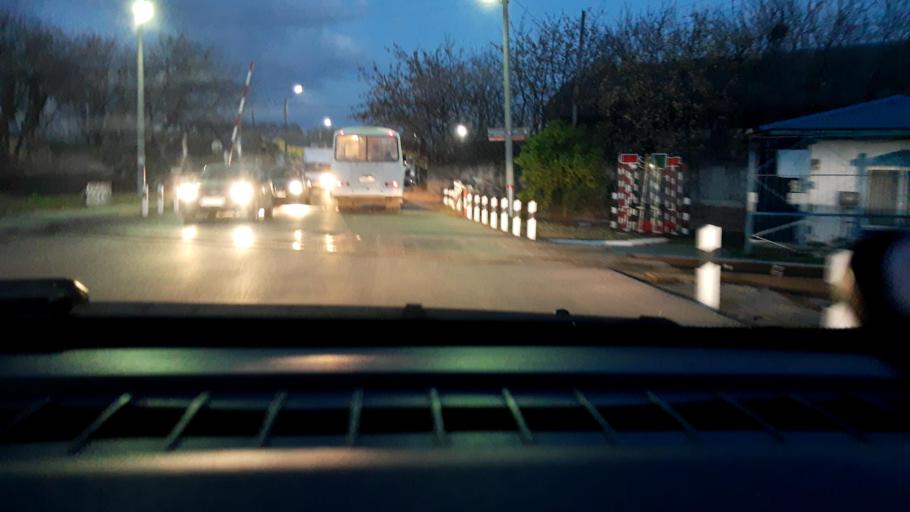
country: RU
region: Nizjnij Novgorod
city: Novaya Balakhna
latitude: 56.4861
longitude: 43.5772
